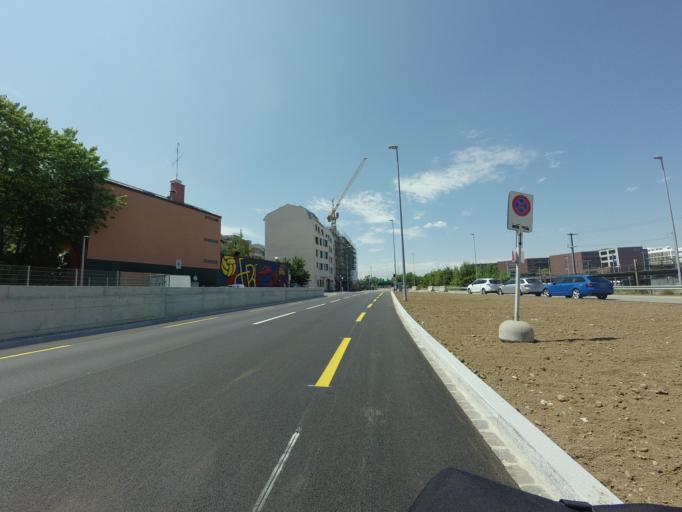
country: CH
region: Basel-City
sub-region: Basel-Stadt
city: Basel
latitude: 47.5466
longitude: 7.5865
